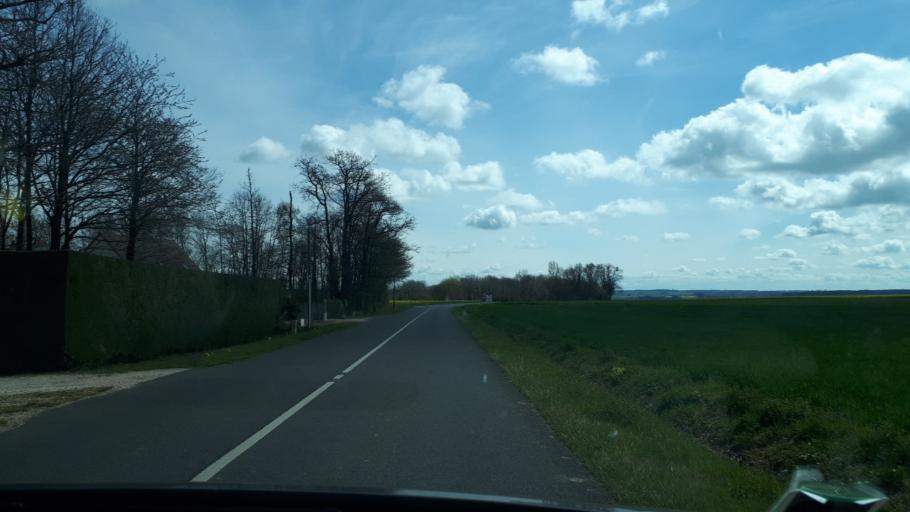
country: FR
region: Centre
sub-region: Departement du Loir-et-Cher
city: Lunay
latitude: 47.8181
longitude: 0.9404
